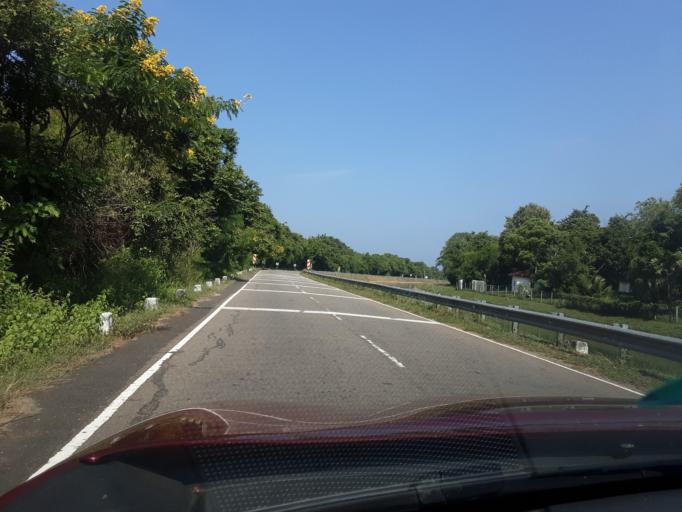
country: LK
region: Uva
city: Badulla
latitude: 7.2748
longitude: 81.0453
